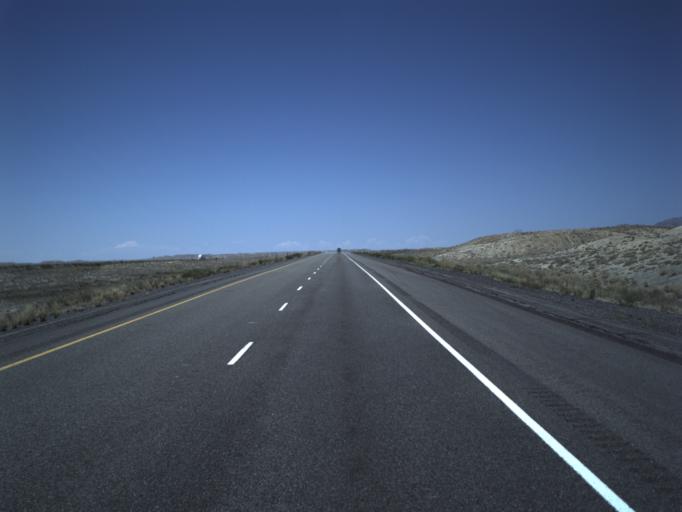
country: US
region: Utah
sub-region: Grand County
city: Moab
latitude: 38.9427
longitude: -109.5383
